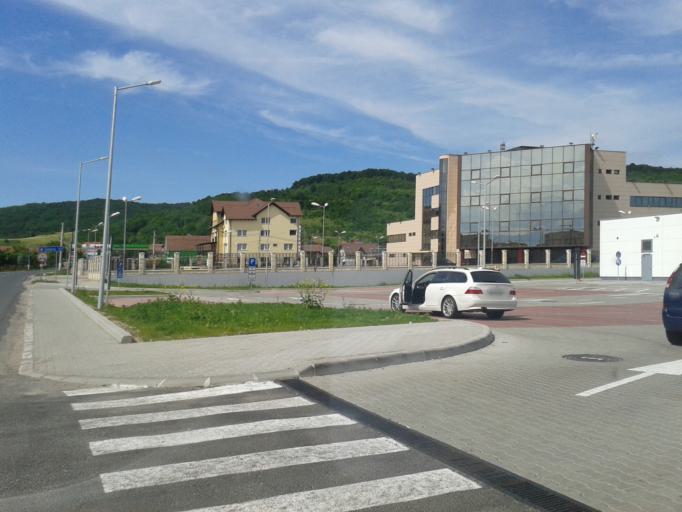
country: RO
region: Hunedoara
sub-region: Oras Hateg
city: Hateg
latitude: 45.6110
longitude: 22.9558
